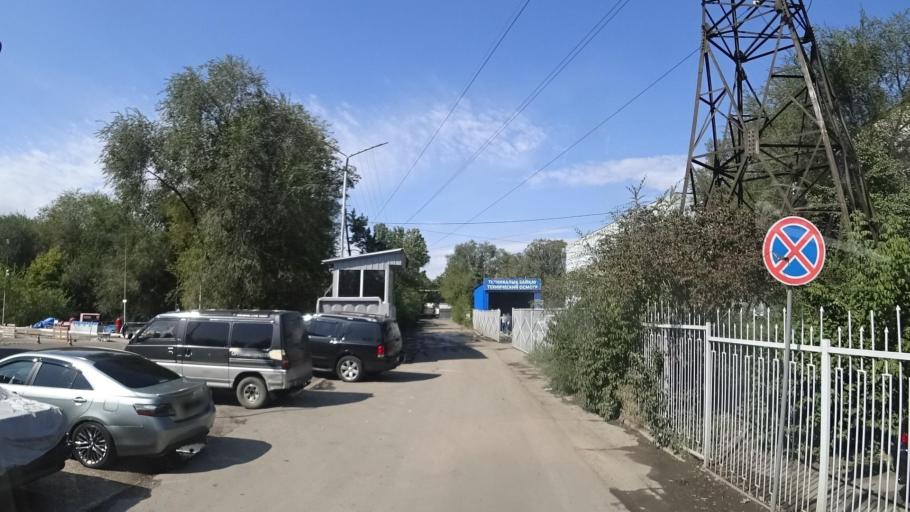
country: KZ
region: Almaty Oblysy
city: Pervomayskiy
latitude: 43.3332
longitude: 76.9785
